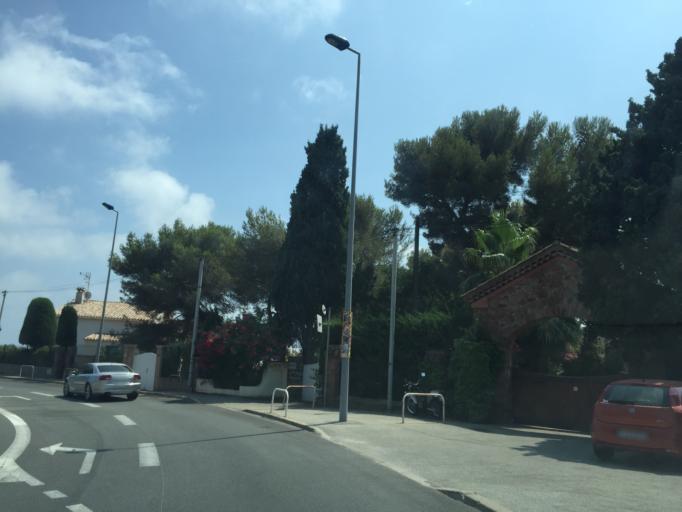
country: FR
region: Provence-Alpes-Cote d'Azur
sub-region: Departement du Var
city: Saint-Raphael
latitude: 43.4265
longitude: 6.8710
